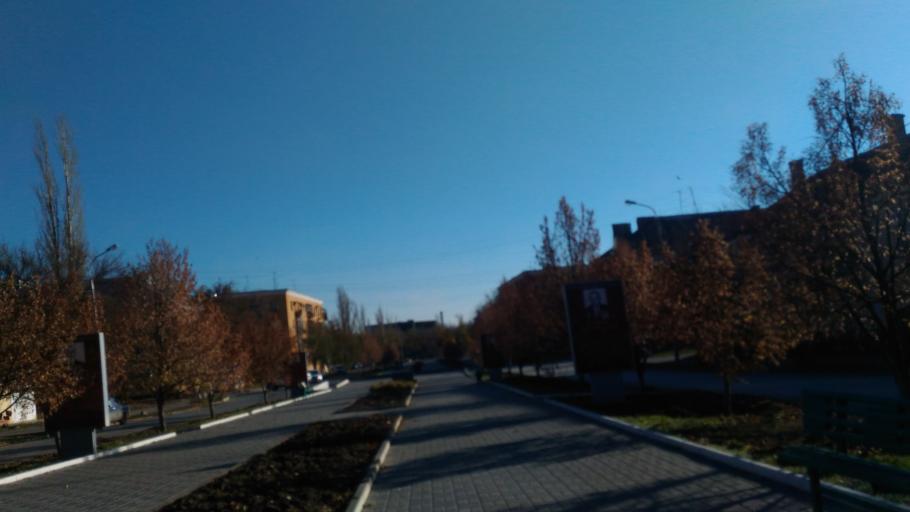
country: RU
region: Volgograd
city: Volgograd
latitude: 48.6616
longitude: 44.4446
